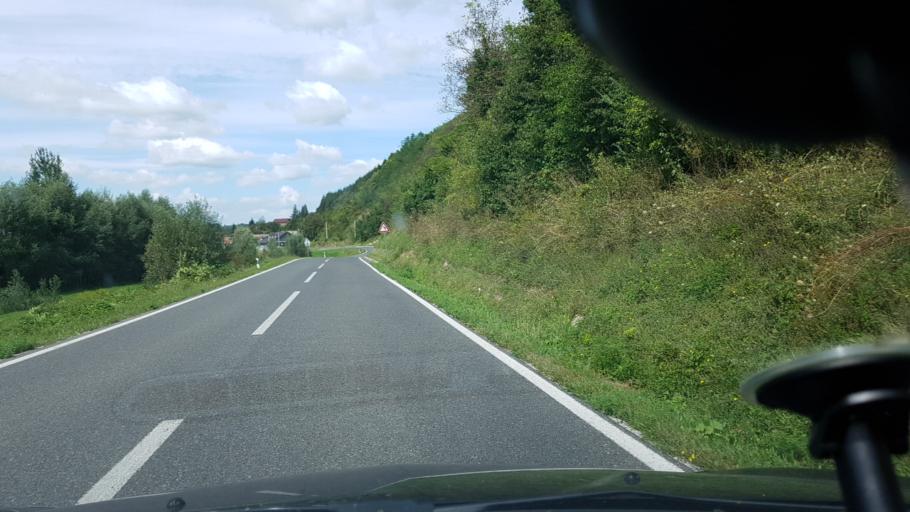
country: HR
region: Varazdinska
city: Lepoglava
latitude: 46.2184
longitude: 15.9973
